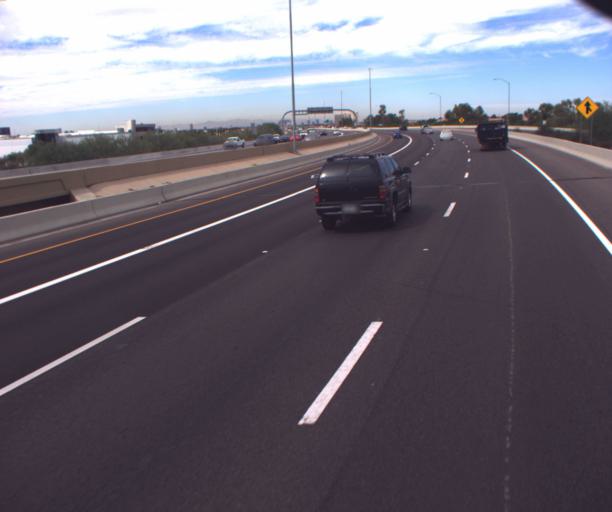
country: US
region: Arizona
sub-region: Maricopa County
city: Tempe Junction
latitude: 33.4549
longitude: -111.9714
